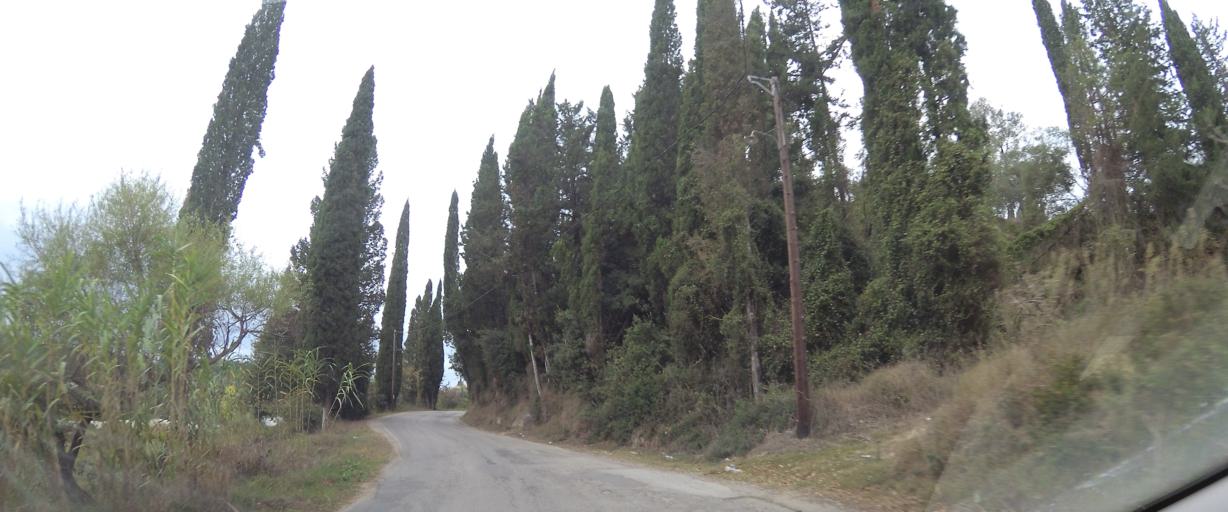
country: GR
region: Ionian Islands
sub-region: Nomos Kerkyras
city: Agios Georgis
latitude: 39.7491
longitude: 19.6841
